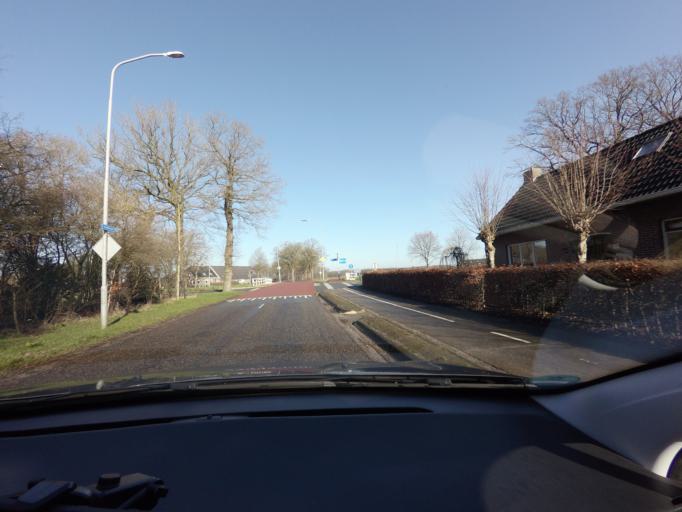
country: NL
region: Drenthe
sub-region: Gemeente Assen
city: Assen
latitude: 52.8853
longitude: 6.5860
